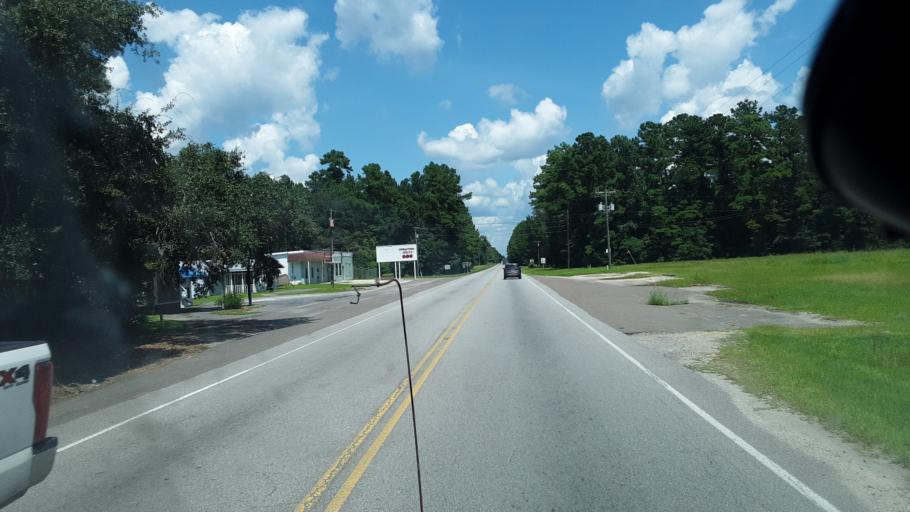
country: US
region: South Carolina
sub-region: Williamsburg County
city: Andrews
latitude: 33.2872
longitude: -79.6934
